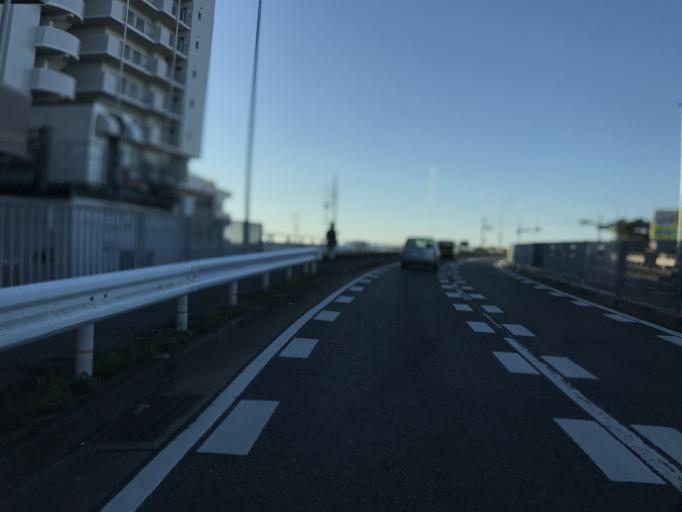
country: JP
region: Aichi
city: Nagoya-shi
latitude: 35.1778
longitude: 136.8486
